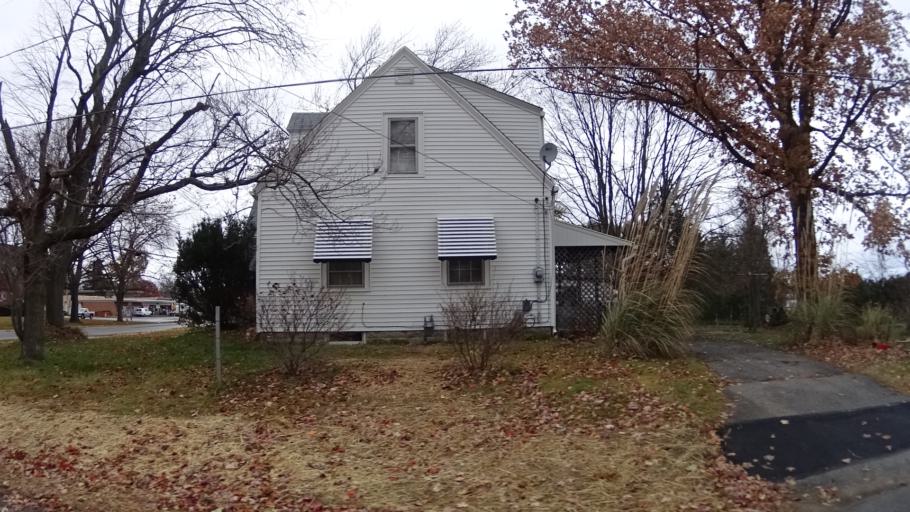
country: US
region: Ohio
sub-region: Lorain County
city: Elyria
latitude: 41.3985
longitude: -82.1310
